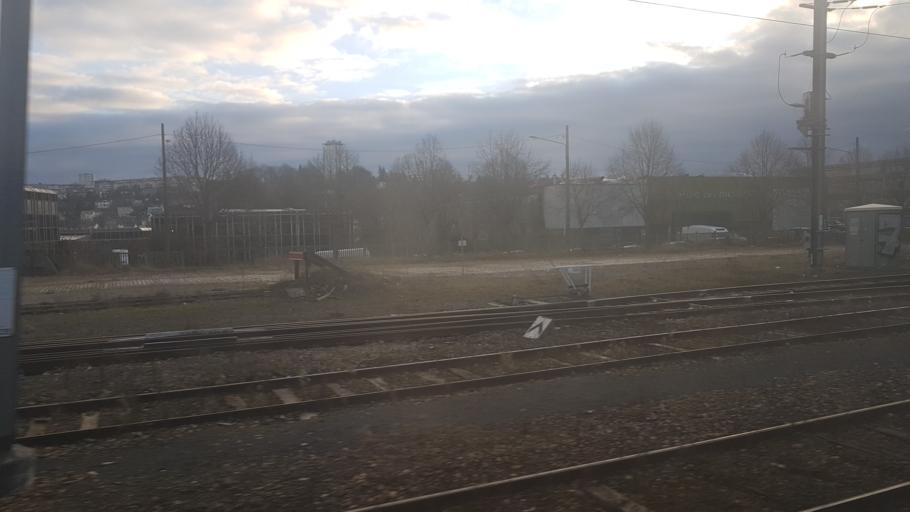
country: FR
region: Lorraine
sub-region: Departement des Vosges
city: Epinal
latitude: 48.1813
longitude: 6.4403
